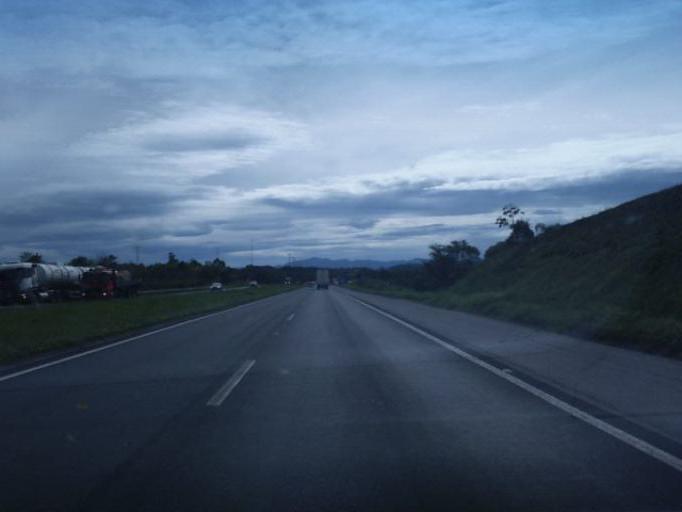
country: BR
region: Sao Paulo
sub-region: Cajati
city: Cajati
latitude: -24.9270
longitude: -48.2688
